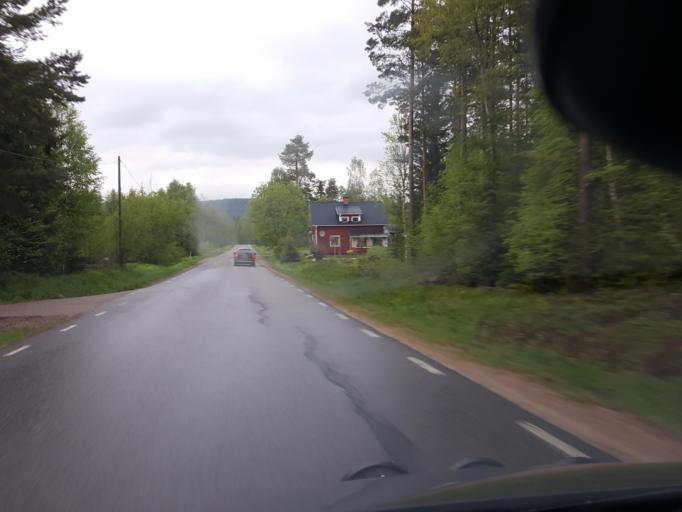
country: SE
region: Gaevleborg
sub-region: Ljusdals Kommun
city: Jaervsoe
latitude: 61.7855
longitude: 16.2173
